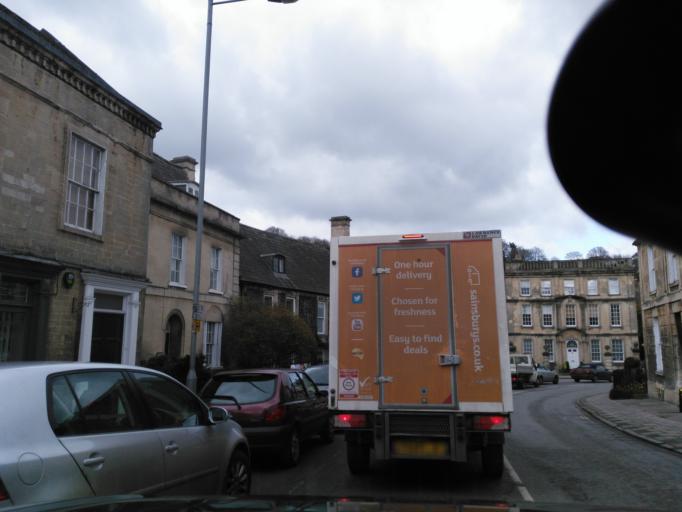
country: GB
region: England
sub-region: Wiltshire
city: Bradford-on-Avon
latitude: 51.3459
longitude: -2.2520
